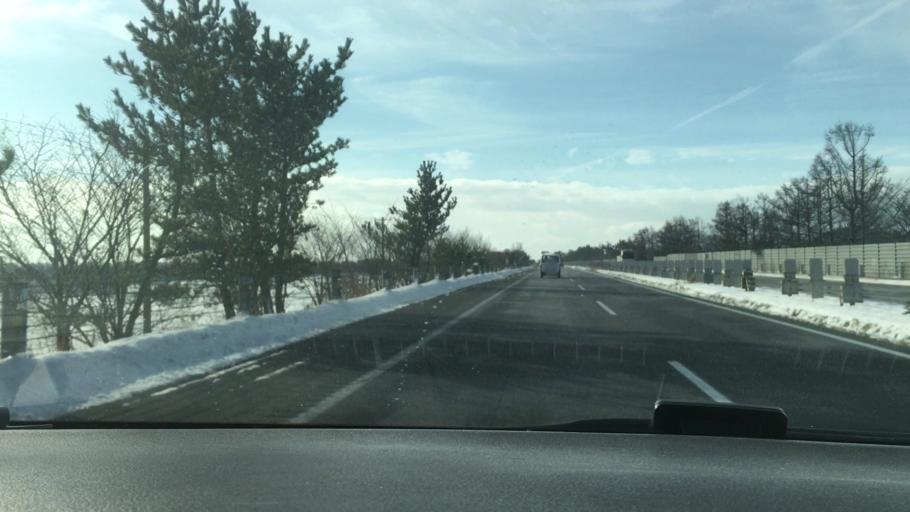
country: JP
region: Iwate
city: Hanamaki
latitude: 39.3657
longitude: 141.0915
